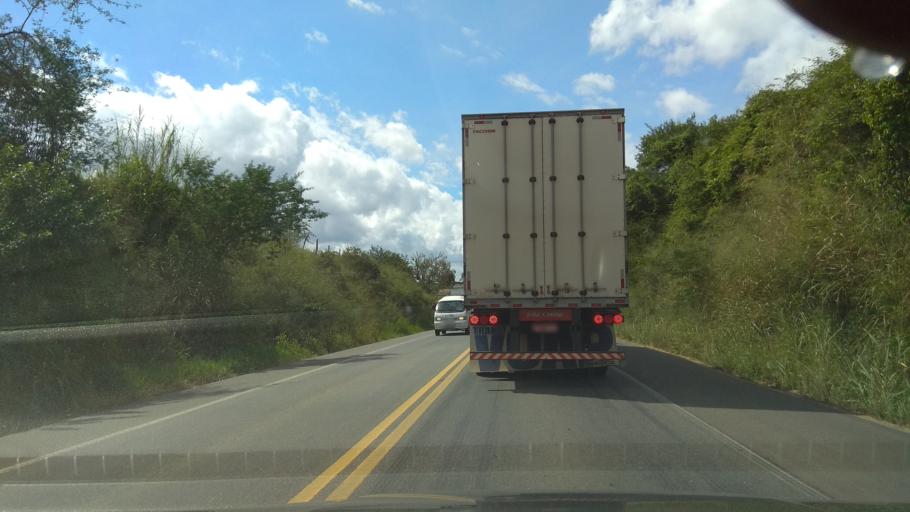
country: BR
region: Bahia
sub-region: Cruz Das Almas
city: Cruz das Almas
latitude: -12.6500
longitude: -39.1191
